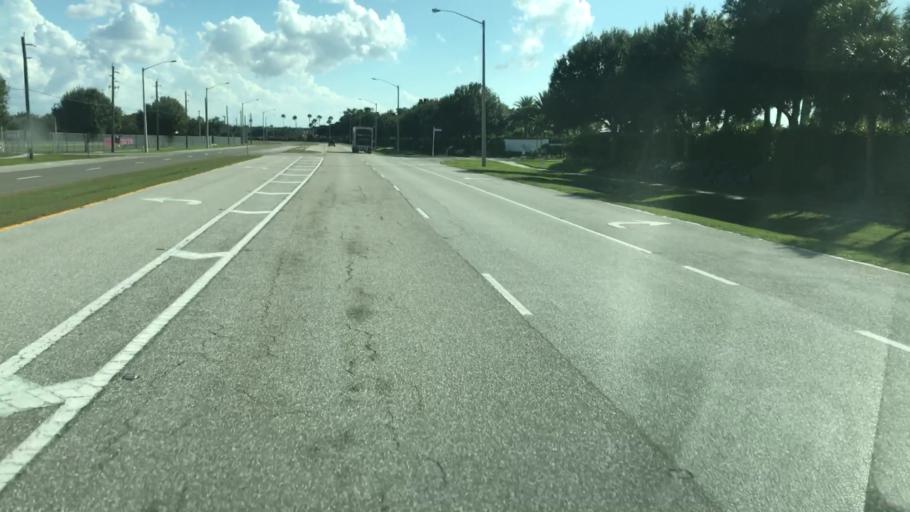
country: US
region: Florida
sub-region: Lee County
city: Fort Myers
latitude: 26.6009
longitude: -81.8182
